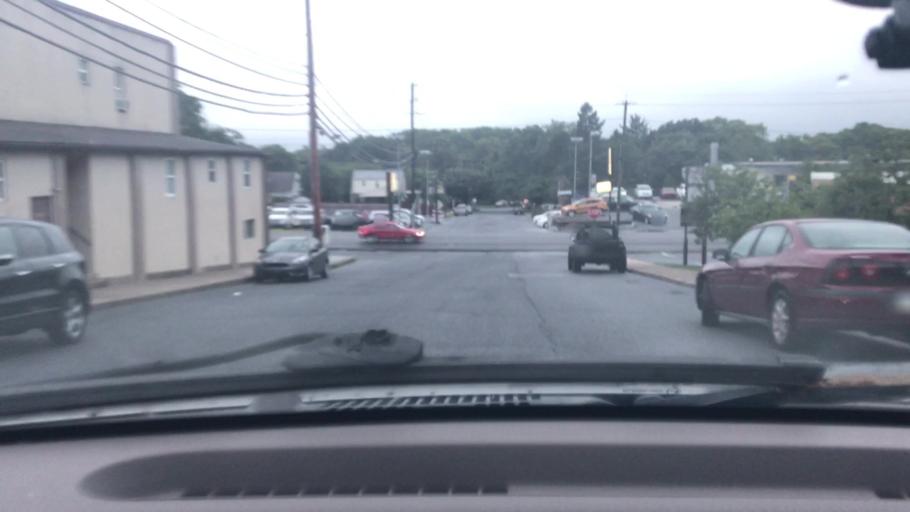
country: US
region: Pennsylvania
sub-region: Dauphin County
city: Palmdale
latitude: 40.2973
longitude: -76.6211
